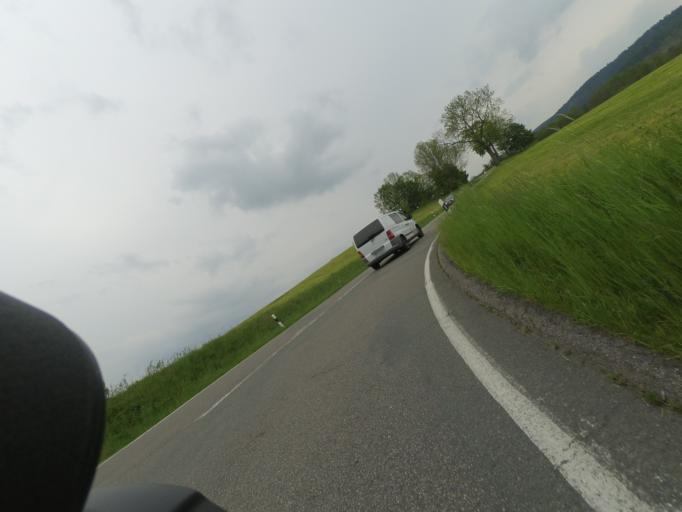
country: DE
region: Saxony
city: Lengefeld
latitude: 50.7345
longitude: 13.1844
